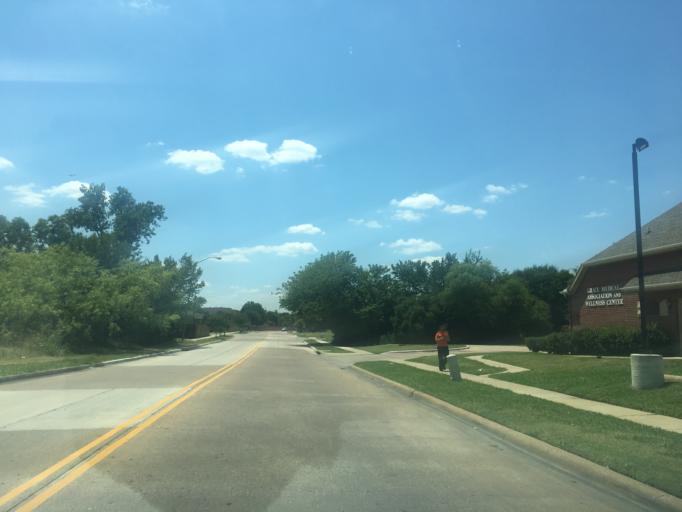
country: US
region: Texas
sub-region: Denton County
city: Lewisville
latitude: 33.0195
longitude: -96.9949
